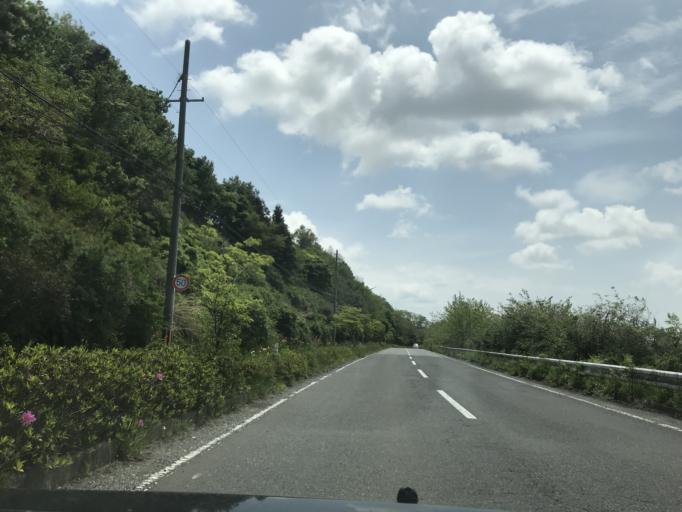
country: JP
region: Miyagi
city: Furukawa
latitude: 38.6665
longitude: 141.0014
